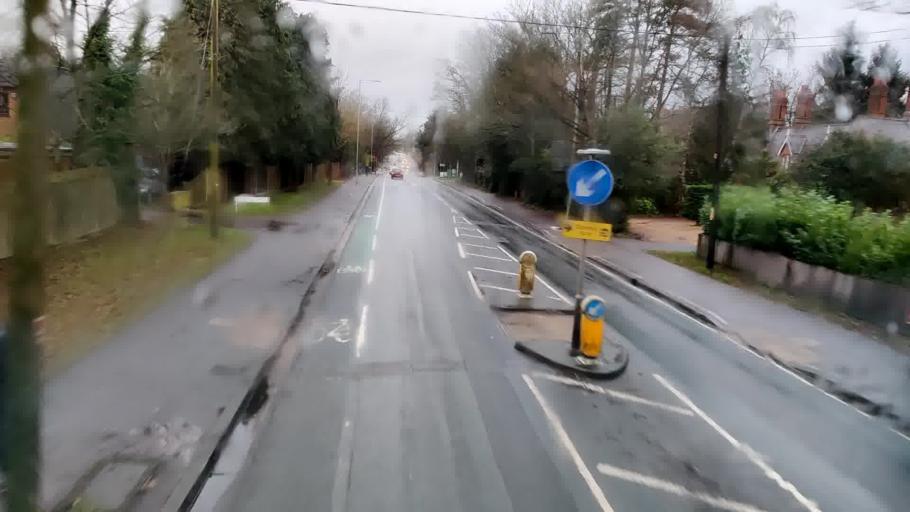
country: GB
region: England
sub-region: Wokingham
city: Winnersh
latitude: 51.4222
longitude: -0.8625
